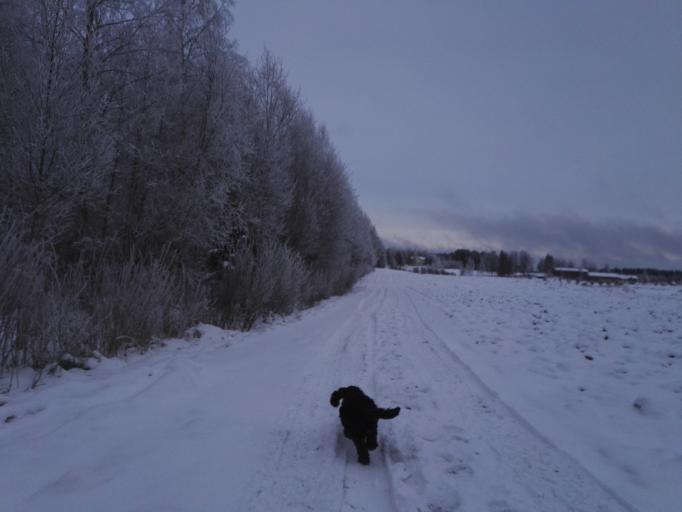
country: FI
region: Satakunta
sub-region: Pohjois-Satakunta
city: Jaemijaervi
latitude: 61.7851
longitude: 22.8714
